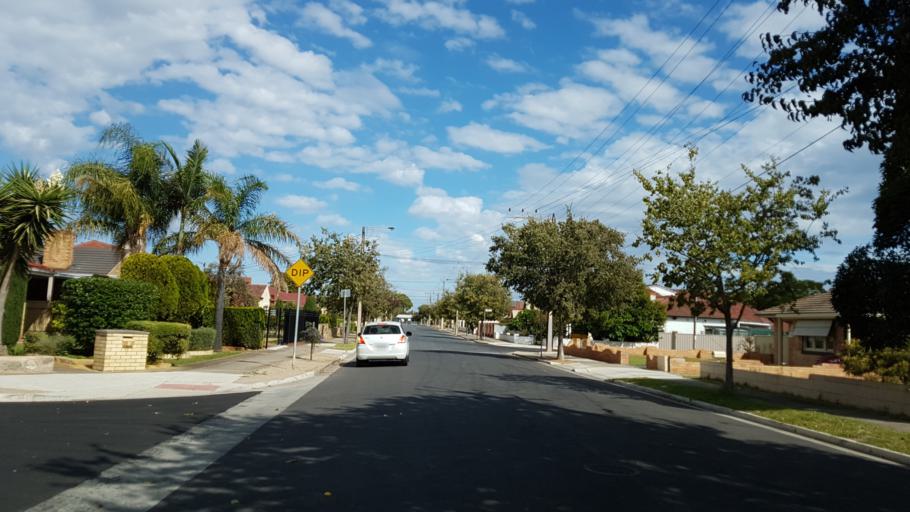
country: AU
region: South Australia
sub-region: City of West Torrens
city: Thebarton
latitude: -34.9262
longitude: 138.5497
